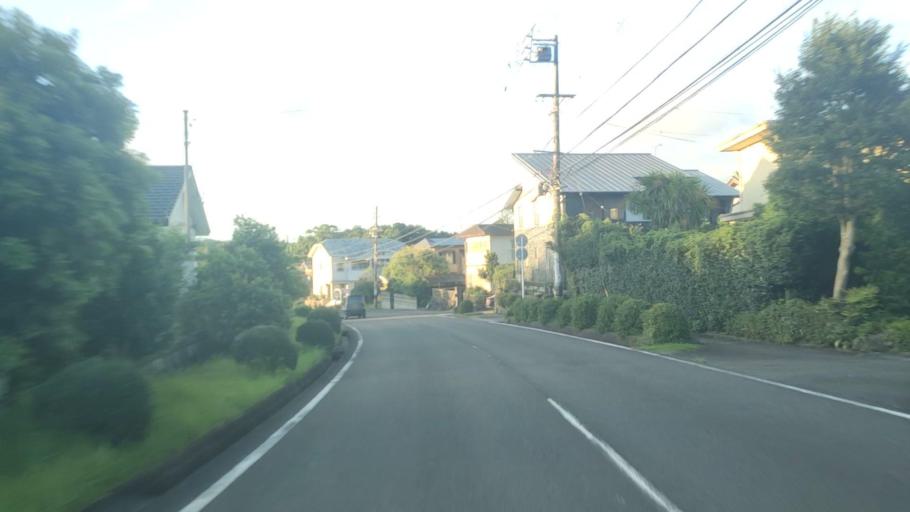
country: JP
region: Mie
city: Toba
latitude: 34.3255
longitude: 136.8224
